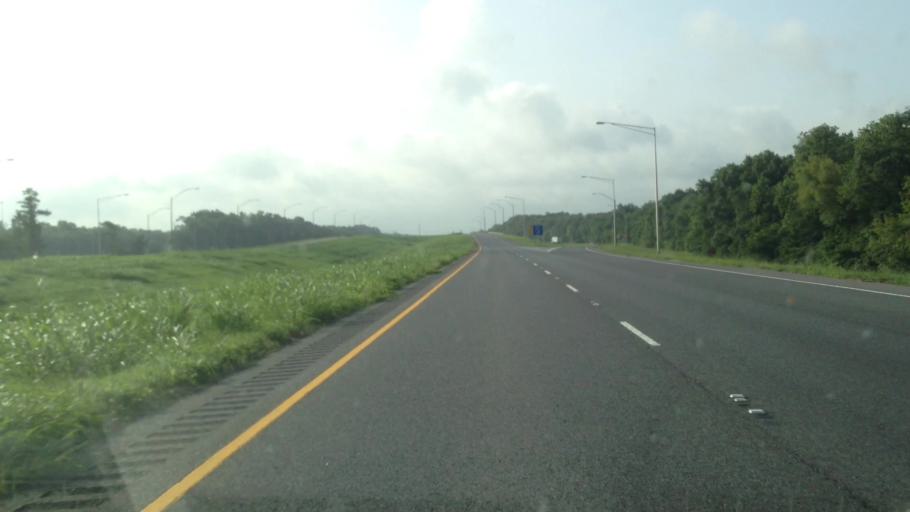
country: US
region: Louisiana
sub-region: Evangeline Parish
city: Ville Platte
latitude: 30.7277
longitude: -92.1244
